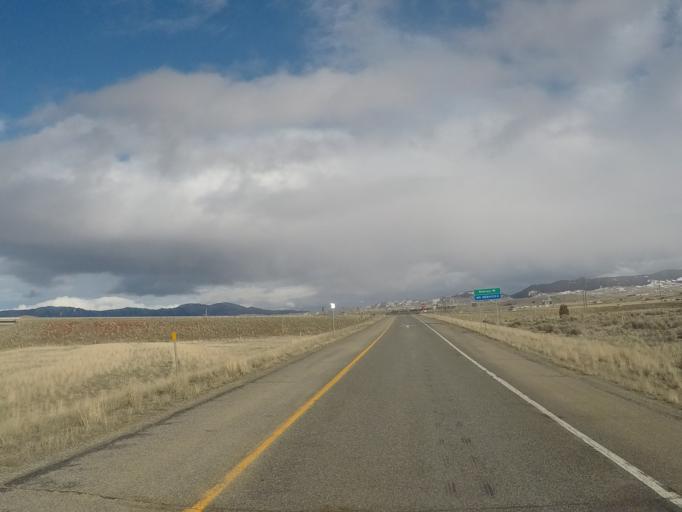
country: US
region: Montana
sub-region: Silver Bow County
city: Butte-Silver Bow (Balance)
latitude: 46.0095
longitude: -112.6864
